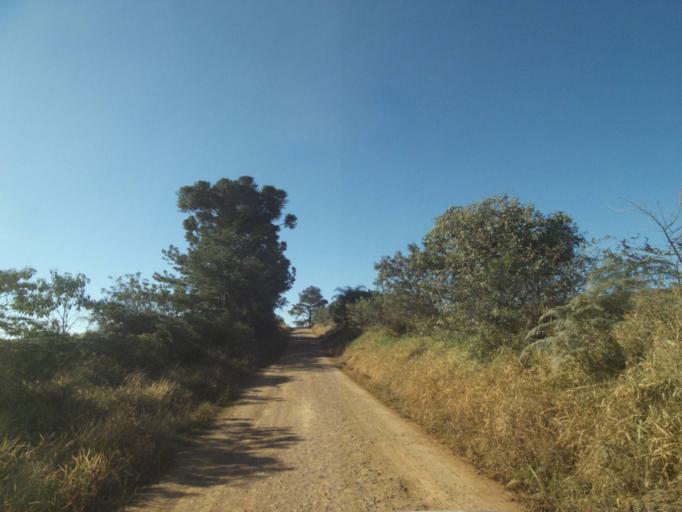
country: BR
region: Parana
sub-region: Tibagi
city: Tibagi
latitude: -24.5439
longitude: -50.5078
